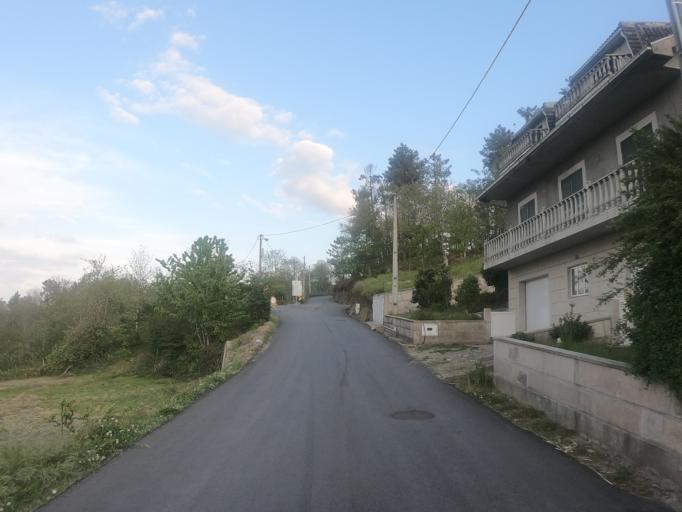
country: PT
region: Vila Real
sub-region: Santa Marta de Penaguiao
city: Santa Marta de Penaguiao
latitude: 41.2776
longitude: -7.8153
